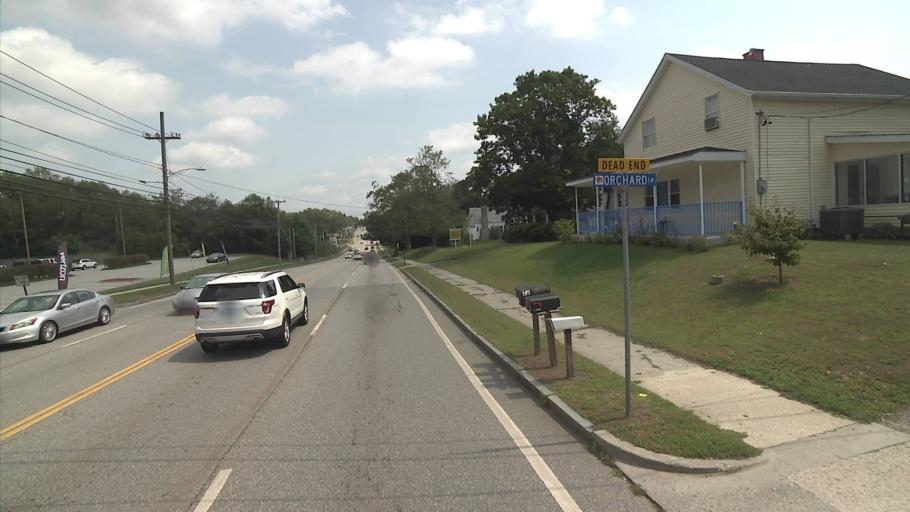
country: US
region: Connecticut
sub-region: New London County
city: Norwich
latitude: 41.5122
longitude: -72.1107
